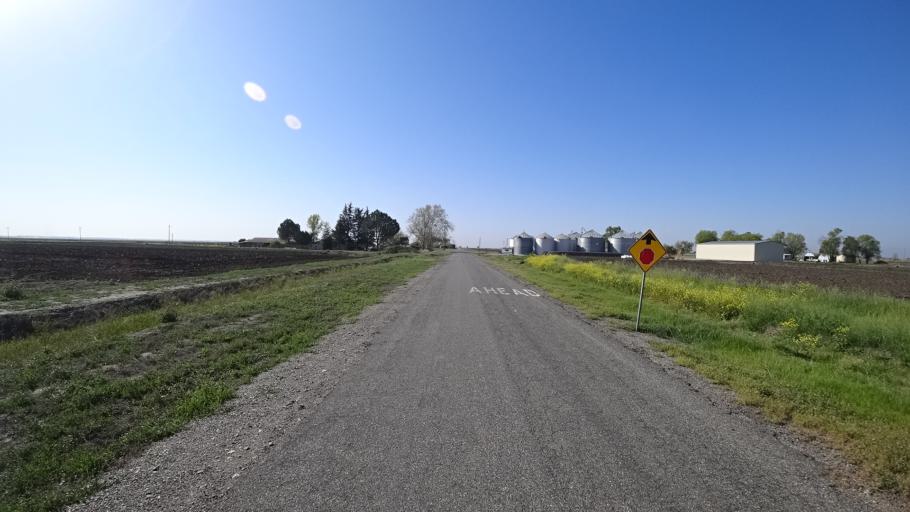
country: US
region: California
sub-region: Glenn County
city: Willows
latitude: 39.5596
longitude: -122.0841
